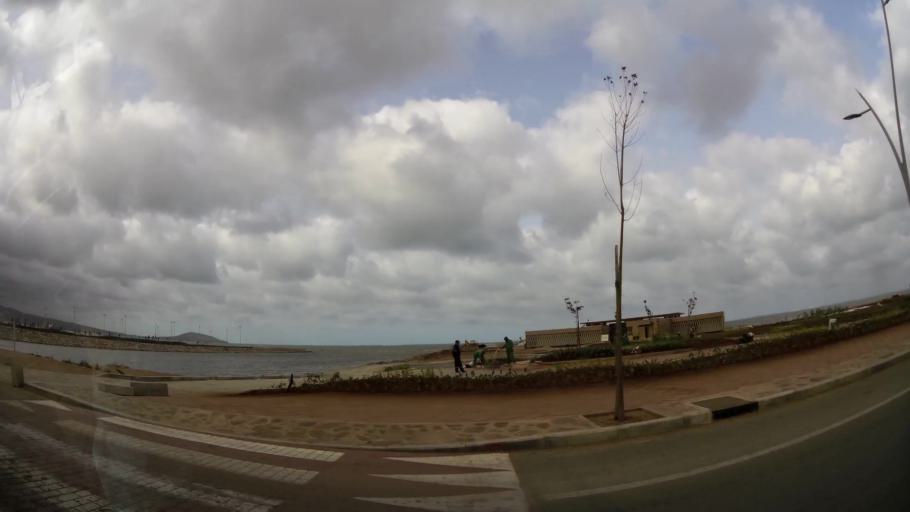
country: MA
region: Oriental
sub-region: Nador
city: Nador
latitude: 35.1613
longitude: -2.9074
